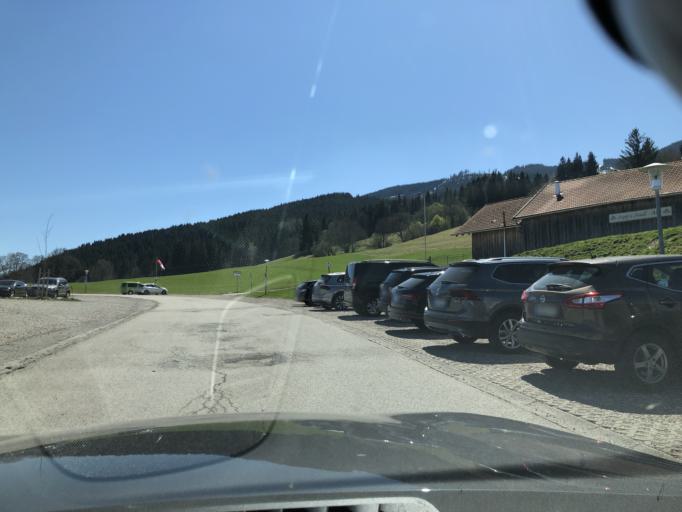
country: DE
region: Bavaria
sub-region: Swabia
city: Nesselwang
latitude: 47.6182
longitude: 10.4985
